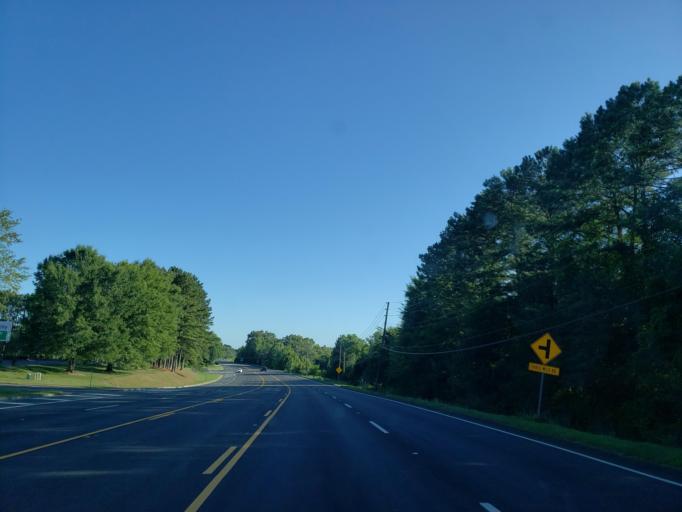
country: US
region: Georgia
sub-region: Floyd County
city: Rome
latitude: 34.3015
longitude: -85.1763
